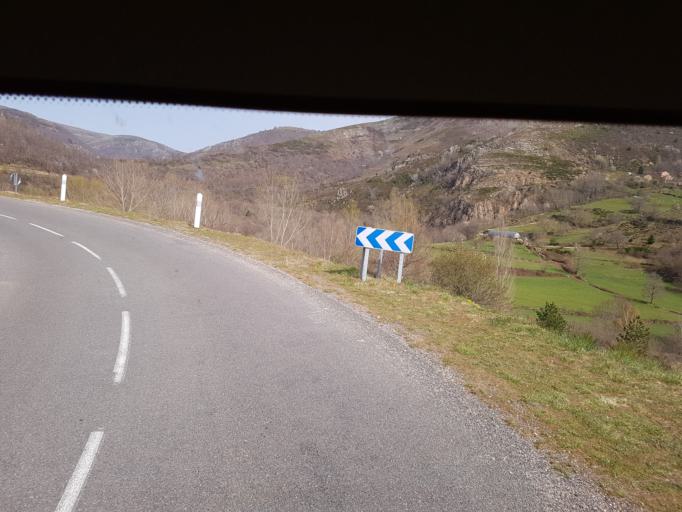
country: FR
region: Languedoc-Roussillon
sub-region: Departement de la Lozere
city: Florac
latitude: 44.3554
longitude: 3.6597
